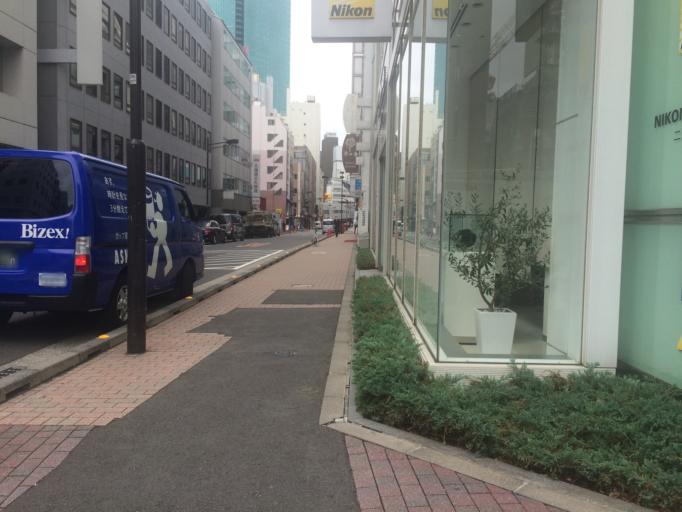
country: JP
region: Tokyo
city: Tokyo
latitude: 35.6689
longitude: 139.7638
